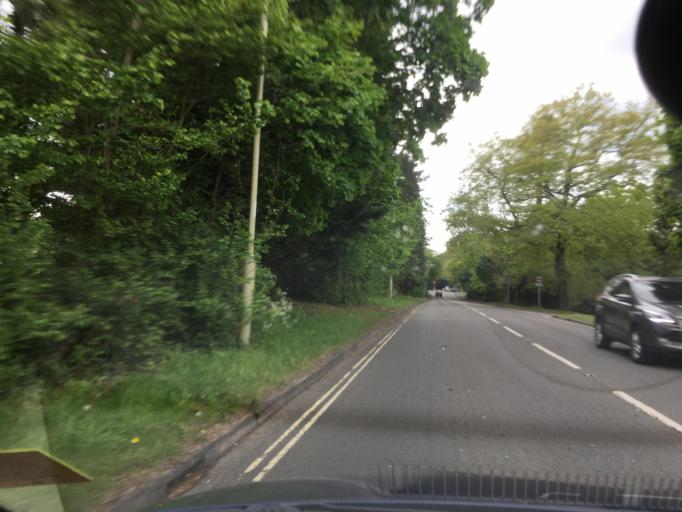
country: GB
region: England
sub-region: Bracknell Forest
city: Sandhurst
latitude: 51.3257
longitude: -0.7753
